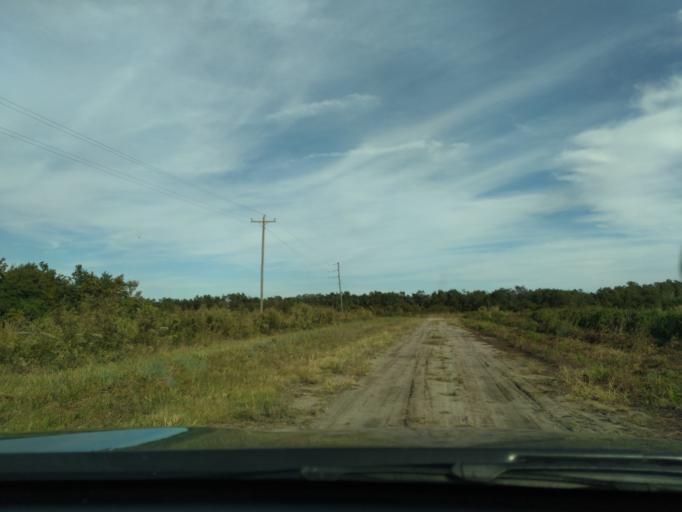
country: US
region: North Carolina
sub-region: Beaufort County
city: Belhaven
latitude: 35.6895
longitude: -76.5264
